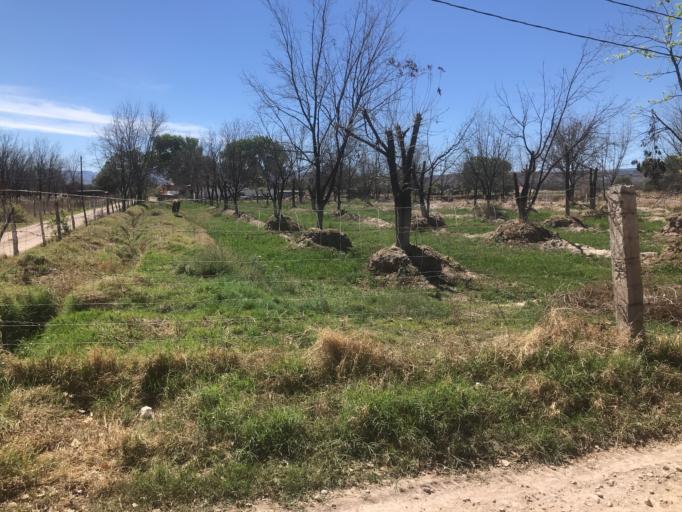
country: MX
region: Durango
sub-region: Durango
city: Sebastian Lerdo de Tejada
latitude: 23.9766
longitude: -104.6109
